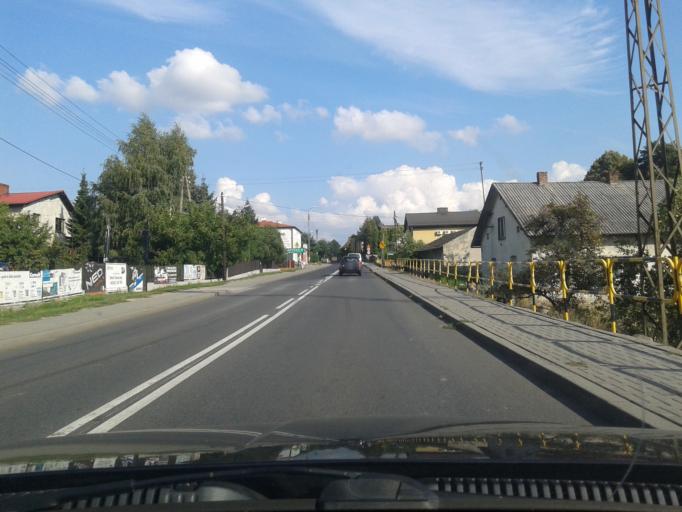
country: PL
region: Silesian Voivodeship
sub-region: Powiat wodzislawski
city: Gorzyce
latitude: 49.9596
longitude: 18.3943
